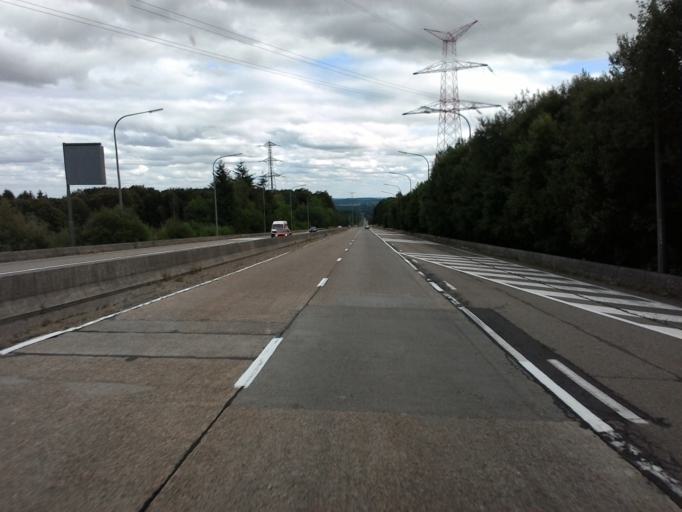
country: BE
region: Wallonia
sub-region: Province du Luxembourg
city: Attert
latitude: 49.7797
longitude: 5.7534
